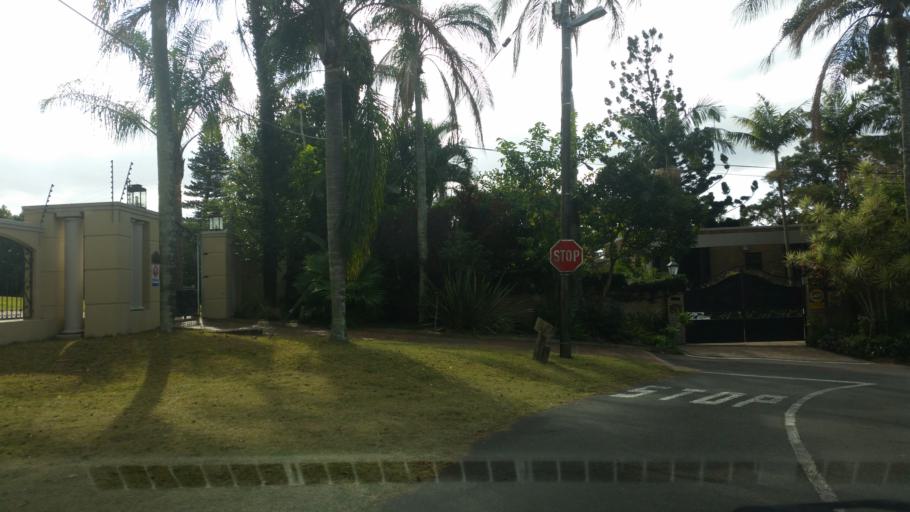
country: ZA
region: KwaZulu-Natal
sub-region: eThekwini Metropolitan Municipality
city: Berea
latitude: -29.8305
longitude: 30.9255
